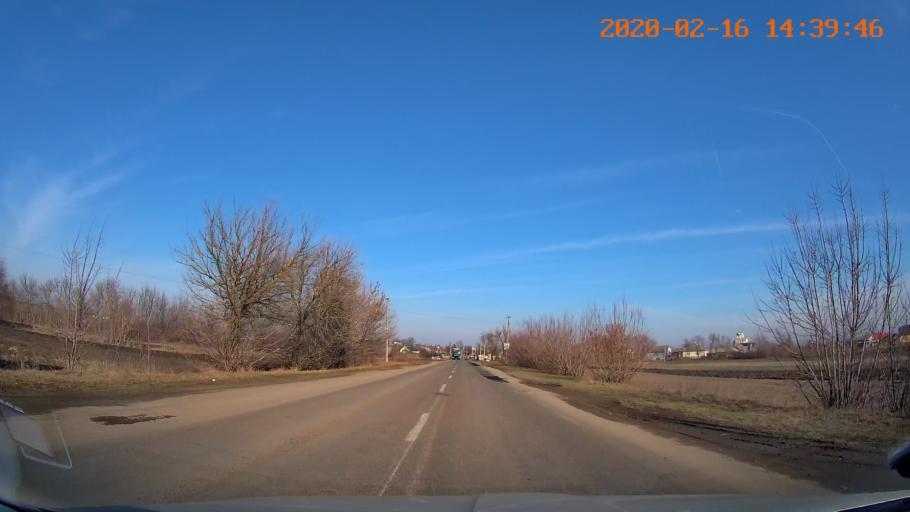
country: RO
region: Botosani
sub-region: Comuna Darabani
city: Bajura
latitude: 48.2462
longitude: 26.5529
